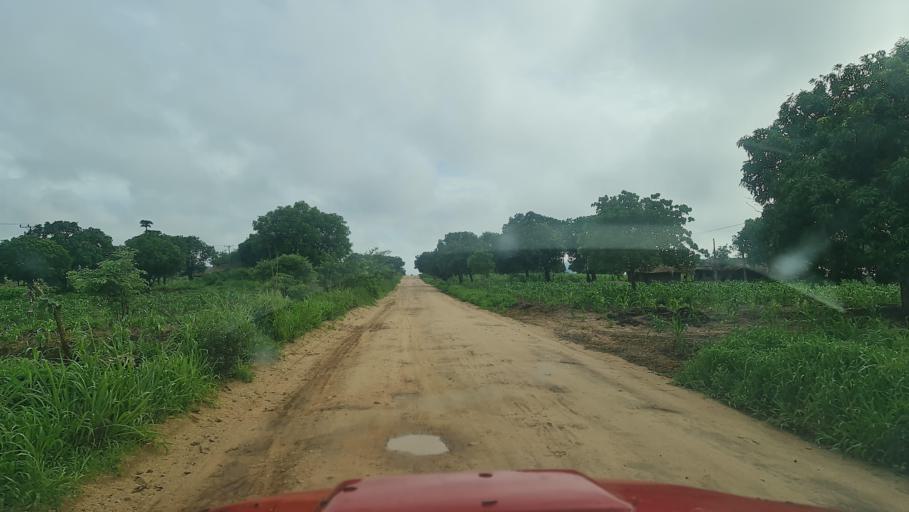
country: MW
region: Southern Region
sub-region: Nsanje District
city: Nsanje
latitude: -17.2902
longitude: 35.6026
